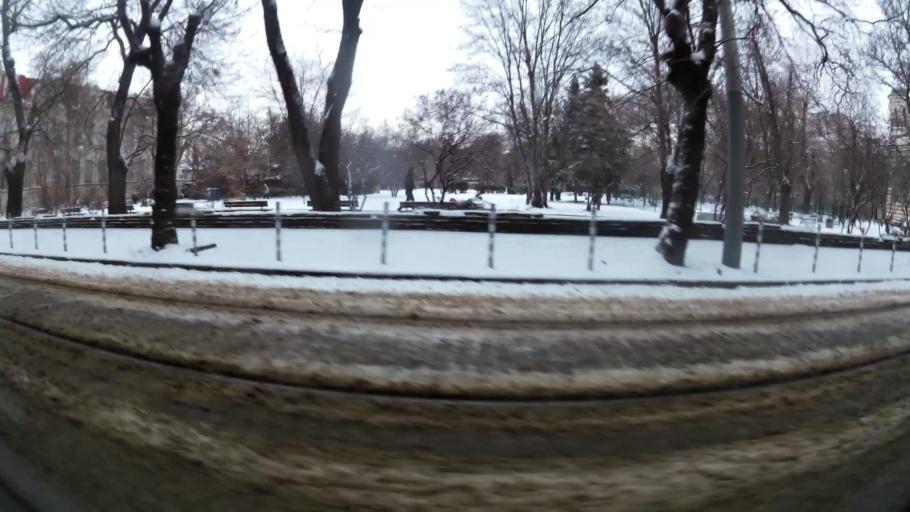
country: BG
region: Sofia-Capital
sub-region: Stolichna Obshtina
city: Sofia
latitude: 42.7015
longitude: 23.3090
